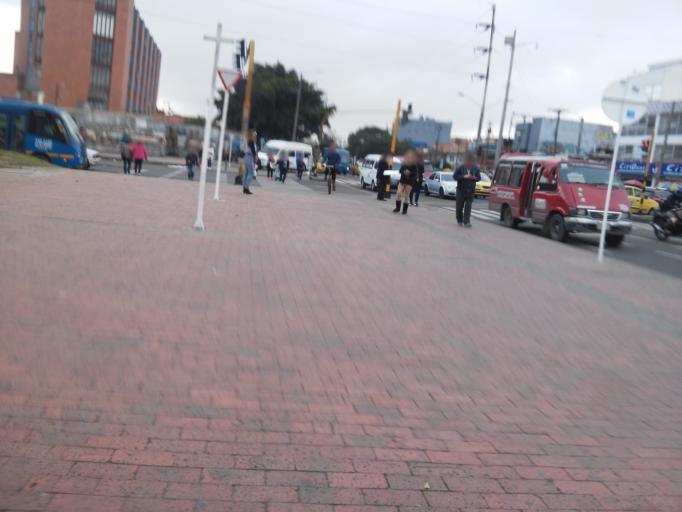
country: CO
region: Bogota D.C.
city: Bogota
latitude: 4.6170
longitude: -74.1525
